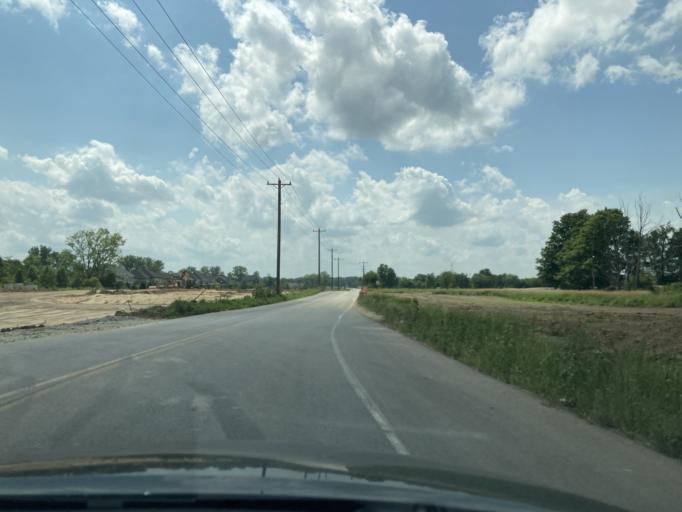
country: US
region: Indiana
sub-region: Boone County
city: Zionsville
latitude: 39.9989
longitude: -86.2244
